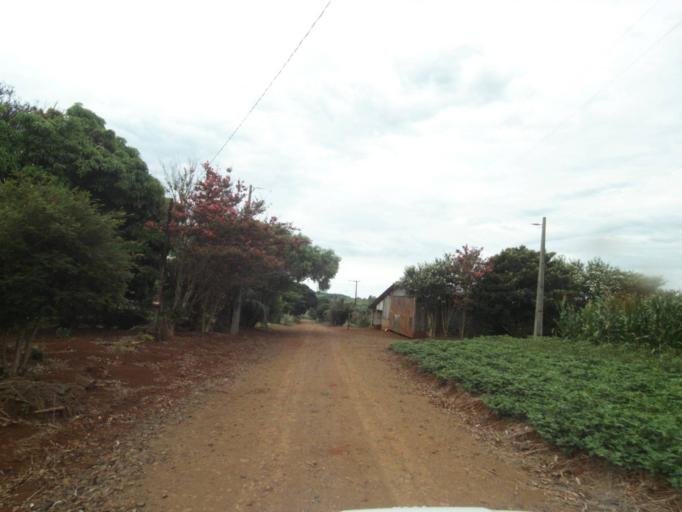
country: BR
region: Parana
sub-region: Guaraniacu
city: Guaraniacu
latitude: -24.9221
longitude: -52.9417
